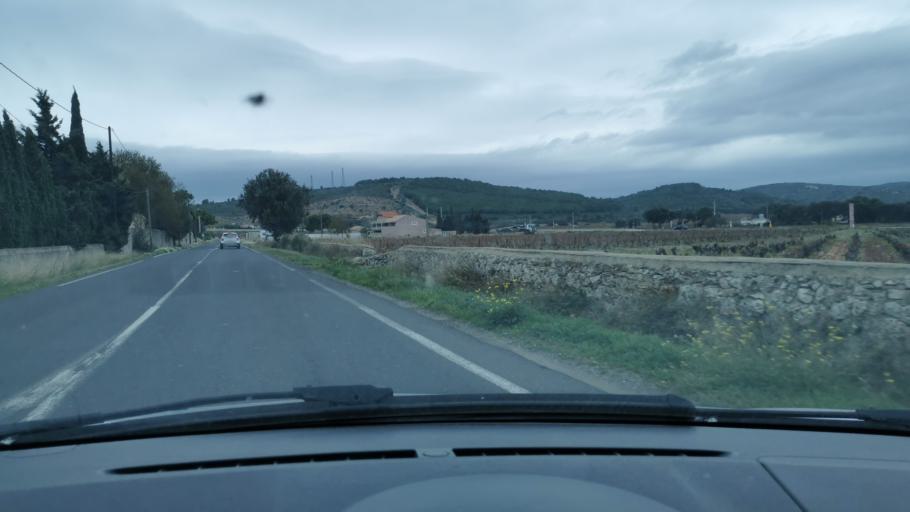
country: FR
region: Languedoc-Roussillon
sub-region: Departement de l'Herault
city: Balaruc-le-Vieux
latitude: 43.4419
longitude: 3.7144
